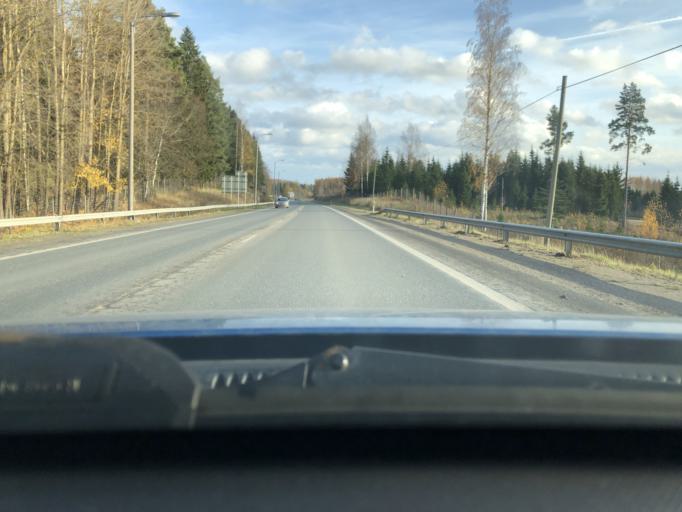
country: FI
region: Pirkanmaa
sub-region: Tampere
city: Kangasala
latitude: 61.4670
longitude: 23.9986
